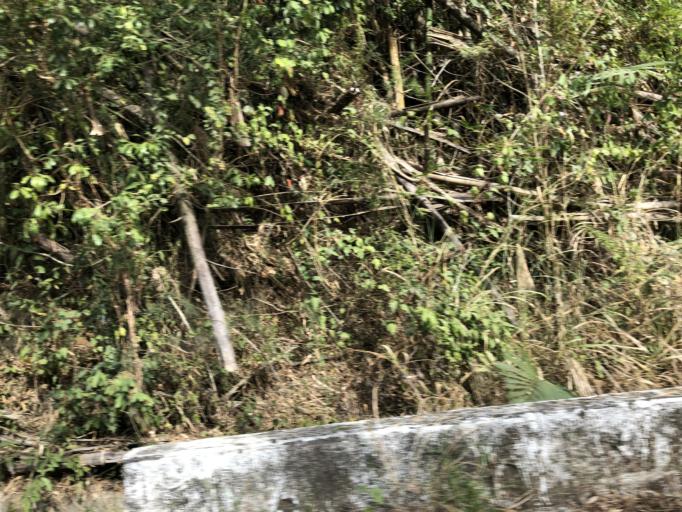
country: TW
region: Taiwan
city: Yujing
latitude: 23.0255
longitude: 120.3954
